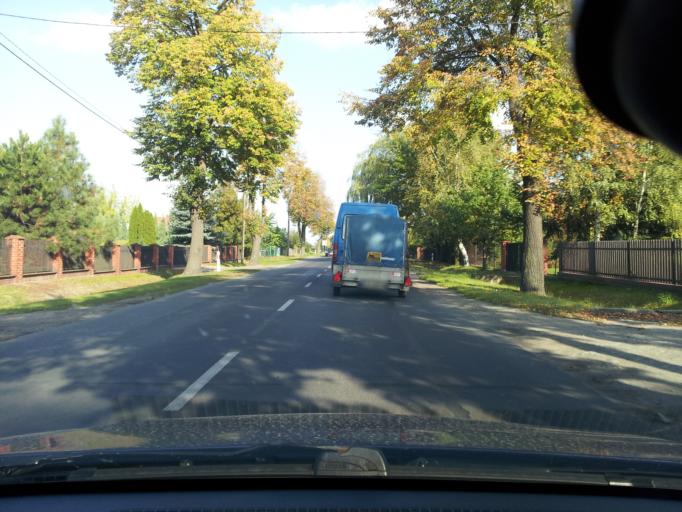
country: PL
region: Kujawsko-Pomorskie
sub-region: Powiat lipnowski
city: Lipno
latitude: 52.8574
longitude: 19.1812
